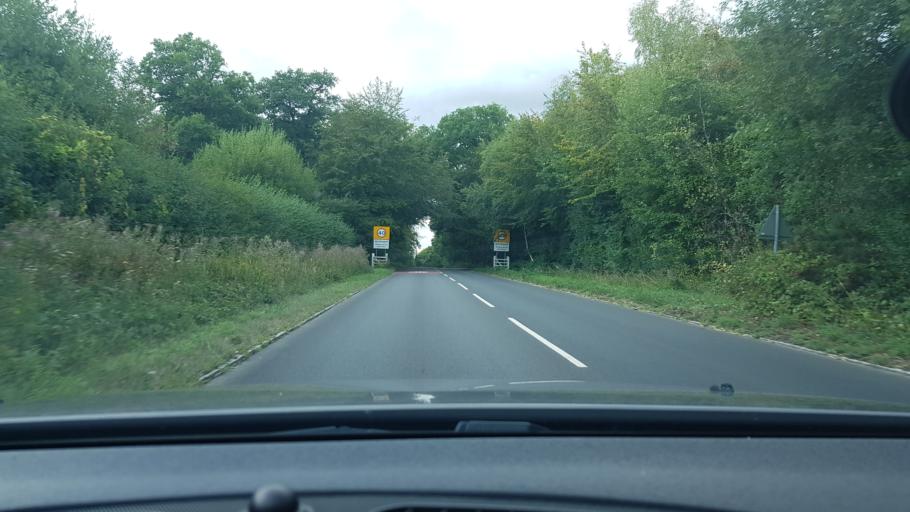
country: GB
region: England
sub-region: West Berkshire
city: Wickham
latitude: 51.4402
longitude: -1.4245
